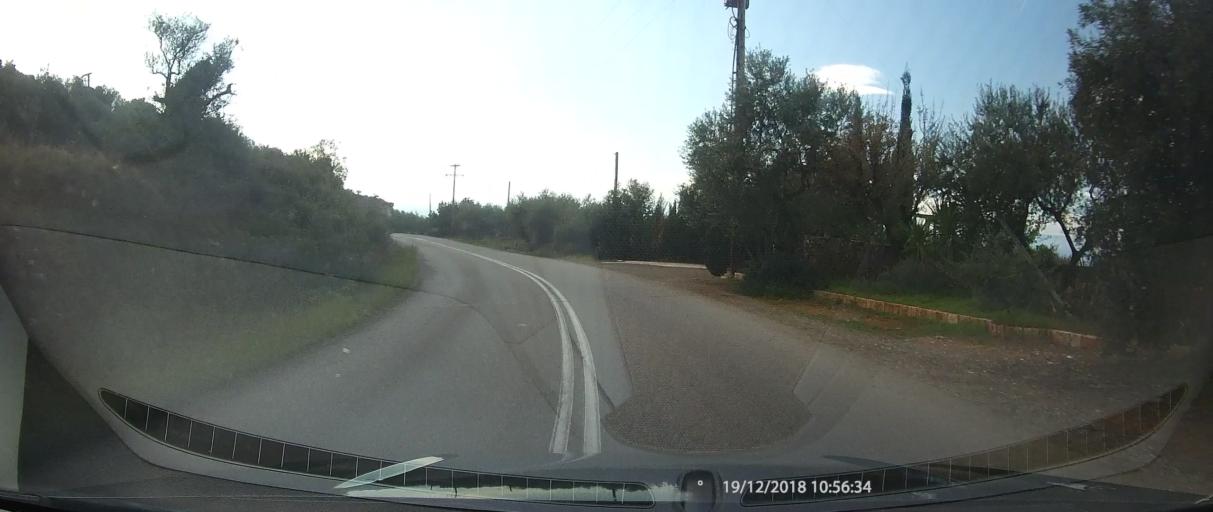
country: GR
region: Peloponnese
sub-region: Nomos Messinias
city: Kardamyli
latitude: 36.9000
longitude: 22.2387
